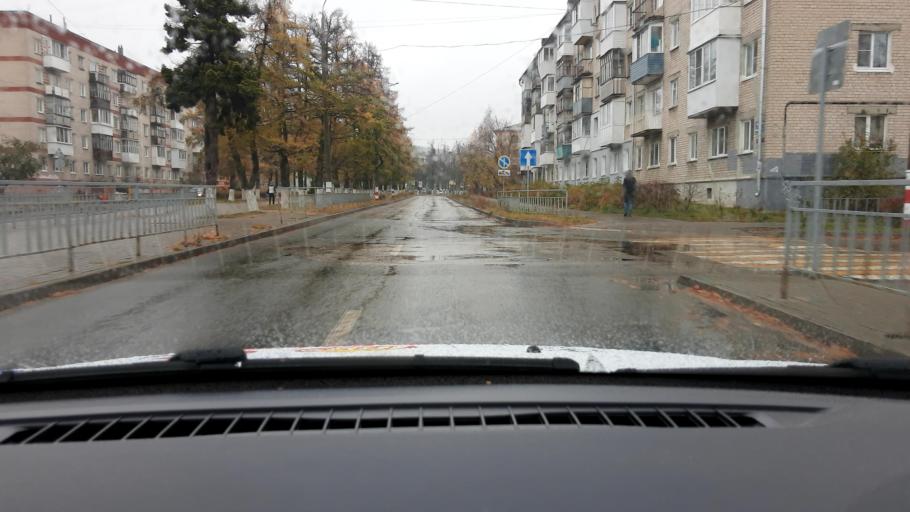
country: RU
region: Nizjnij Novgorod
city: Dzerzhinsk
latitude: 56.2378
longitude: 43.4432
